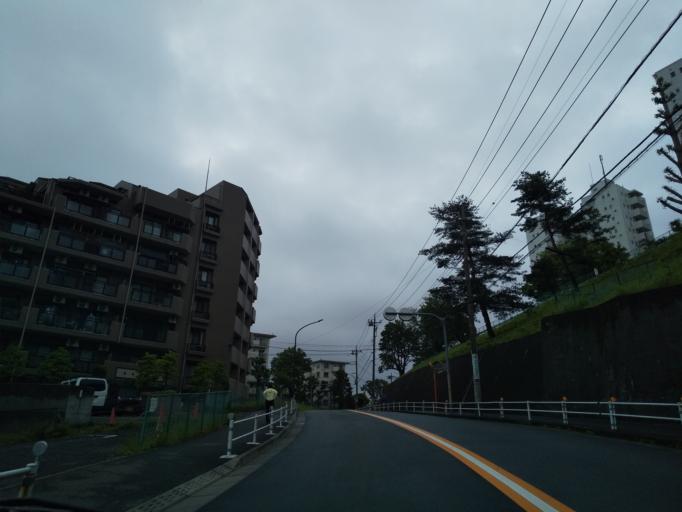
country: JP
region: Tokyo
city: Hino
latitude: 35.6510
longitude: 139.4172
